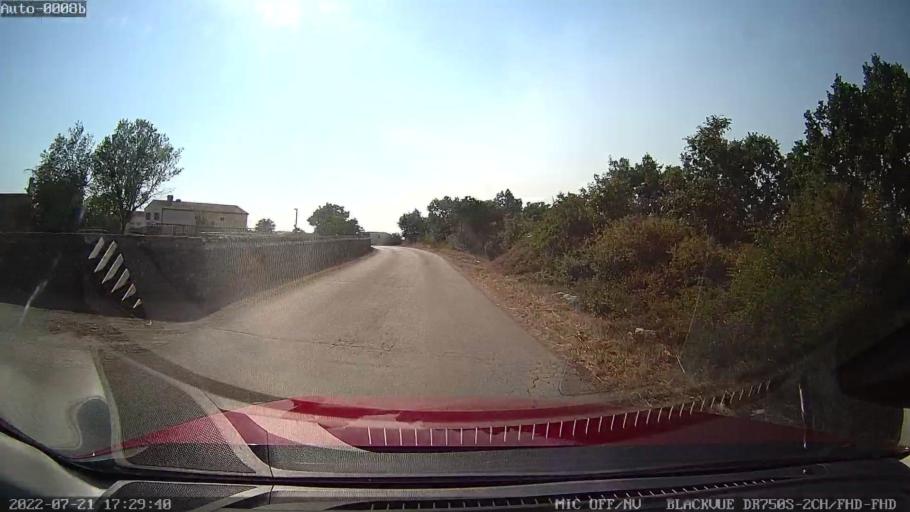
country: HR
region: Istarska
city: Karojba
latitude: 45.1791
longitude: 13.7825
